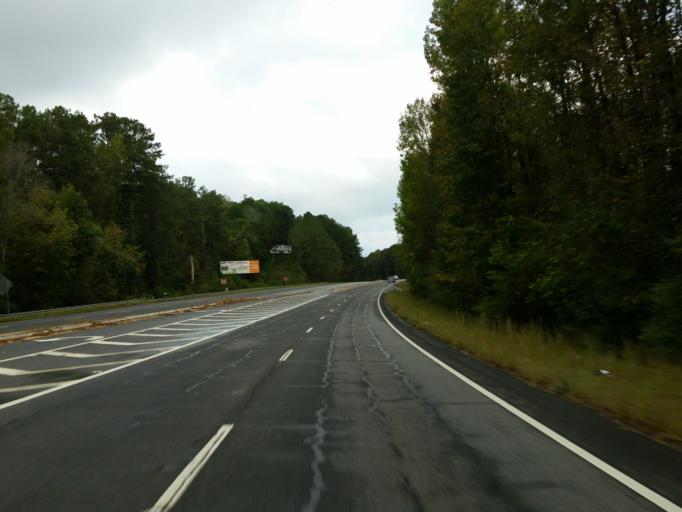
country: US
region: Georgia
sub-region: Bartow County
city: Emerson
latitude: 34.0923
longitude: -84.7401
